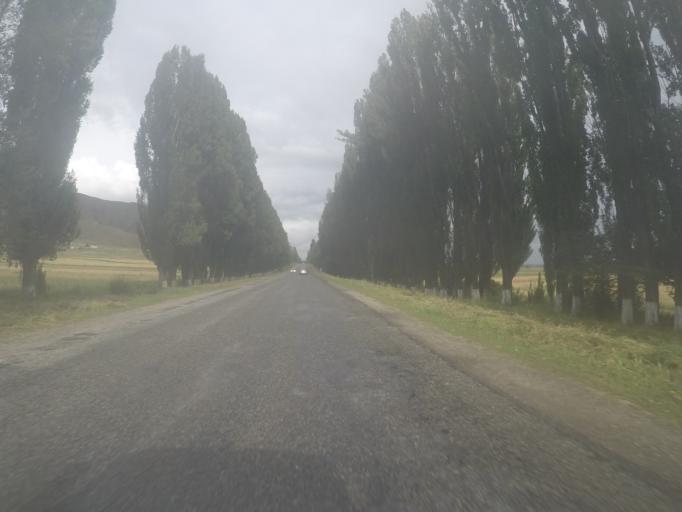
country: KG
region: Ysyk-Koel
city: Tyup
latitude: 42.7426
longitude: 78.0355
